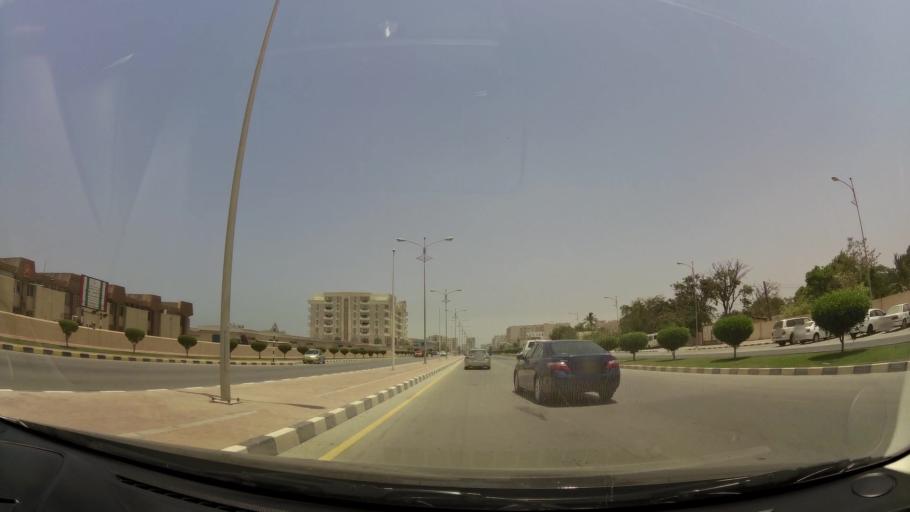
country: OM
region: Zufar
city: Salalah
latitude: 17.0205
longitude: 54.1163
